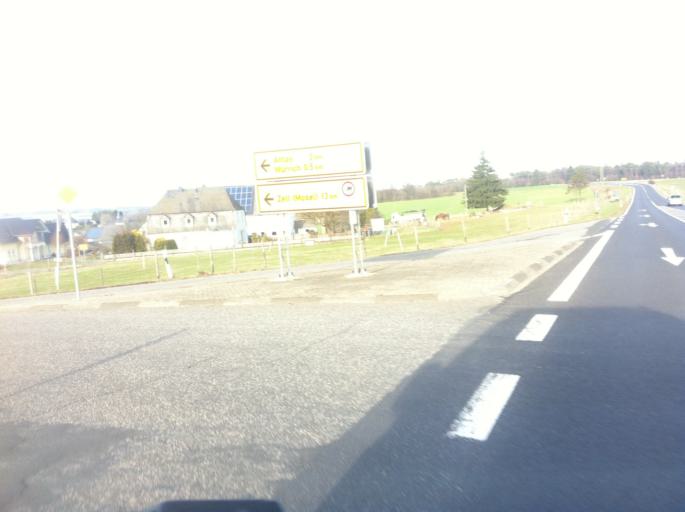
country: DE
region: Rheinland-Pfalz
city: Wurrich
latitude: 49.9717
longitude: 7.2985
